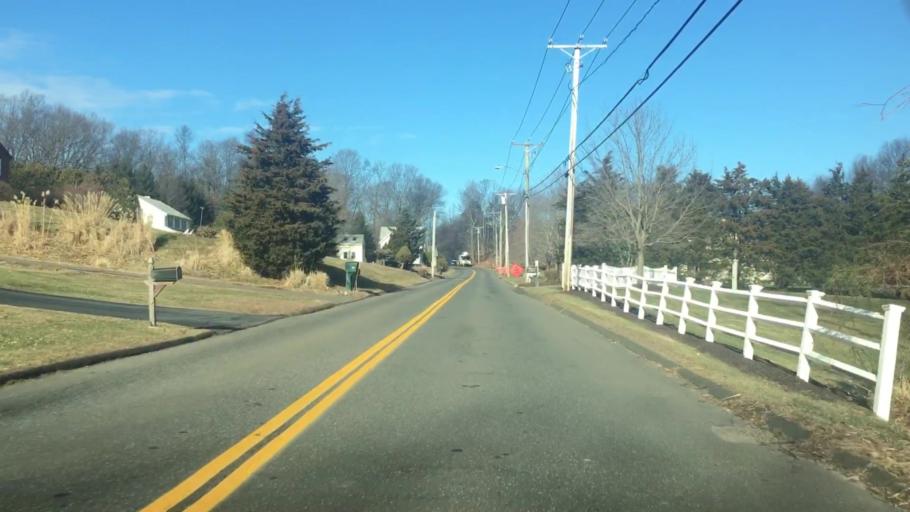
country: US
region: Connecticut
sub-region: Middlesex County
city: Durham
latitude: 41.5144
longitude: -72.6486
